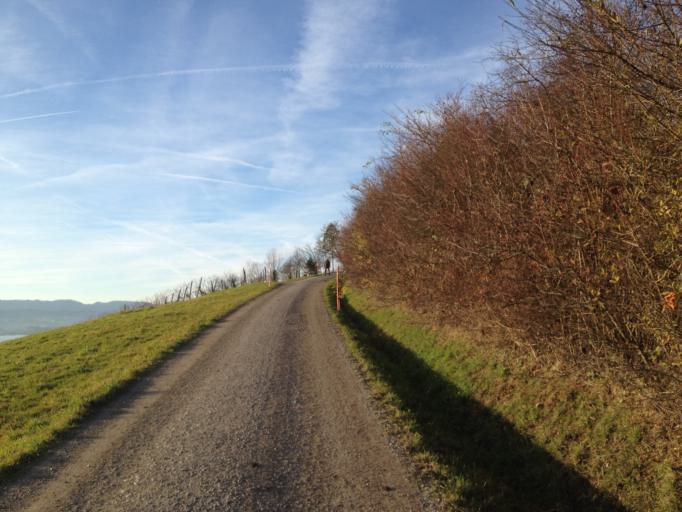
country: CH
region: Zurich
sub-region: Bezirk Meilen
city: Stafa
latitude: 47.2474
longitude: 8.7318
